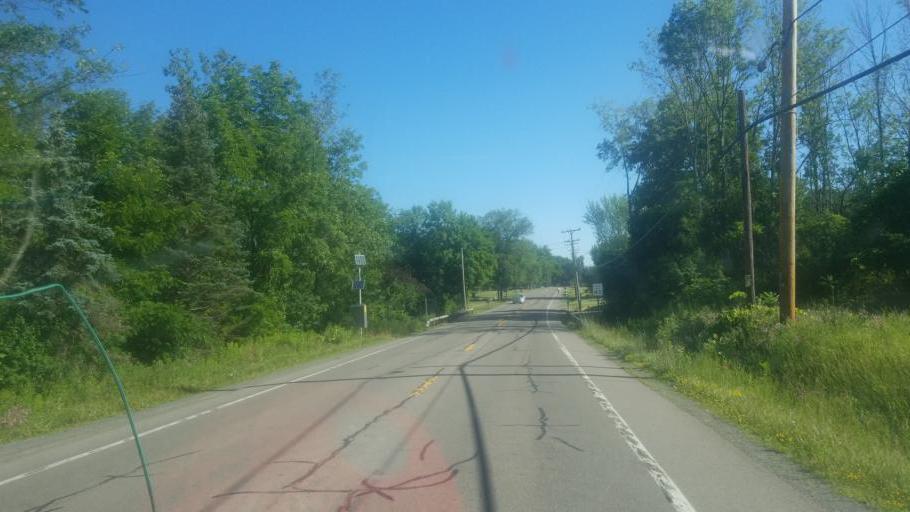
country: US
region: New York
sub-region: Ontario County
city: Canandaigua
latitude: 42.8485
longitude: -77.2554
